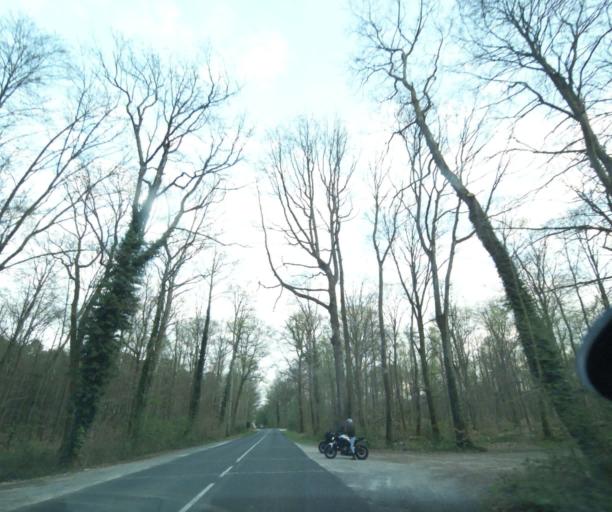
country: FR
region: Ile-de-France
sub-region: Departement de Seine-et-Marne
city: Montigny-sur-Loing
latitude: 48.3509
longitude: 2.7652
